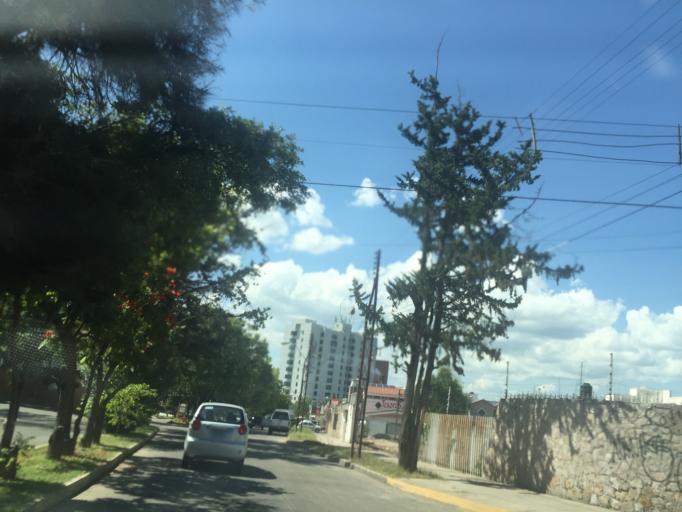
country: MX
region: Guanajuato
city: Leon
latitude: 21.1520
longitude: -101.6974
